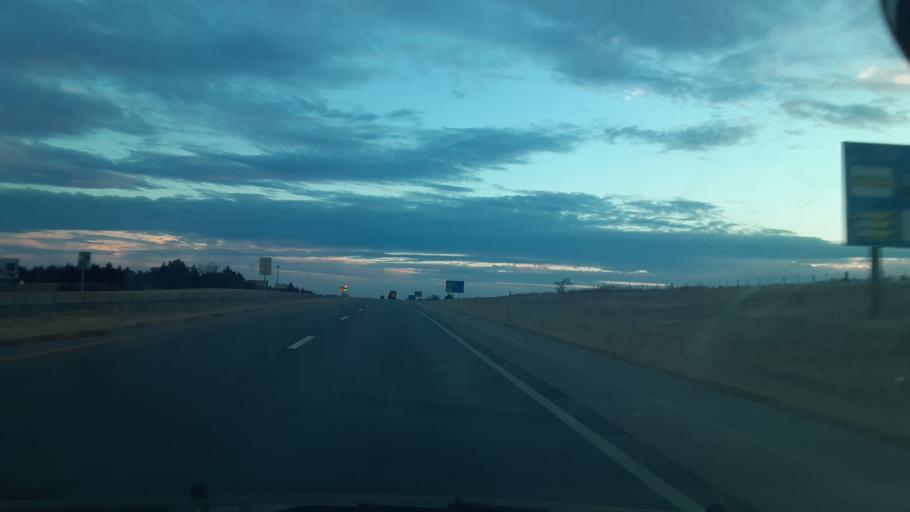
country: US
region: Oklahoma
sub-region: Logan County
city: Guthrie
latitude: 35.8937
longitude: -97.3942
